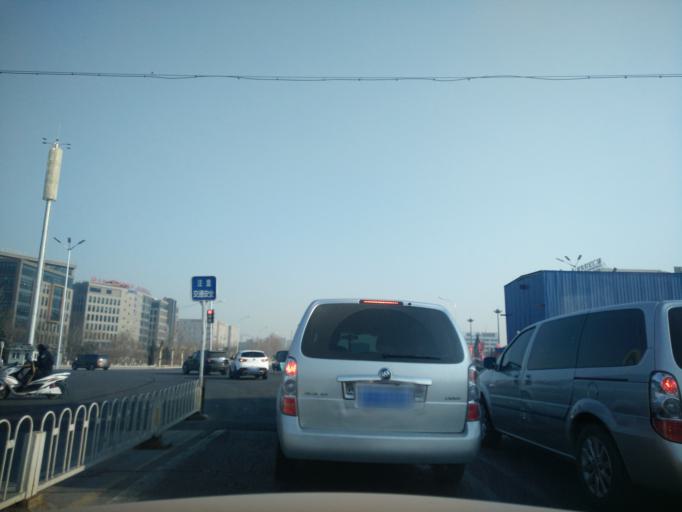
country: CN
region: Beijing
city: Jiugong
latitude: 39.8013
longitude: 116.5239
